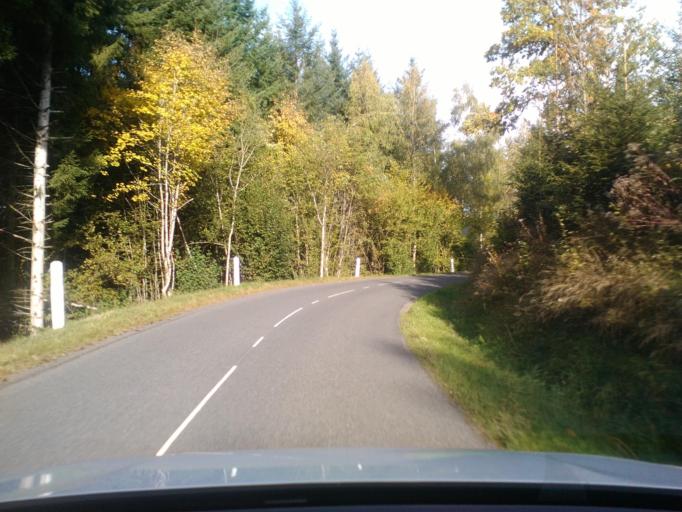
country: FR
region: Lorraine
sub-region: Departement des Vosges
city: Senones
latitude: 48.3728
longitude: 7.0399
